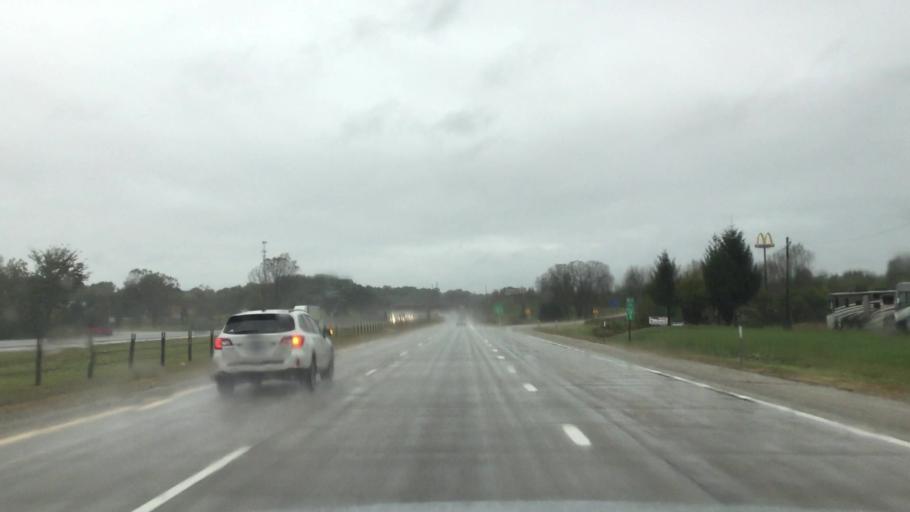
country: US
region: Michigan
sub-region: Berrien County
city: Coloma
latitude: 42.1763
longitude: -86.2998
